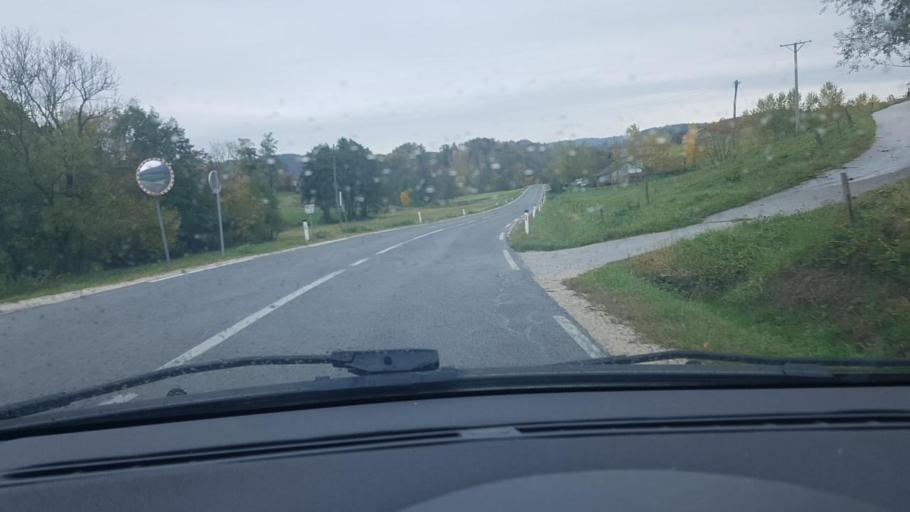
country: SI
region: Rogatec
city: Rogatec
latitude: 46.2585
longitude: 15.7025
